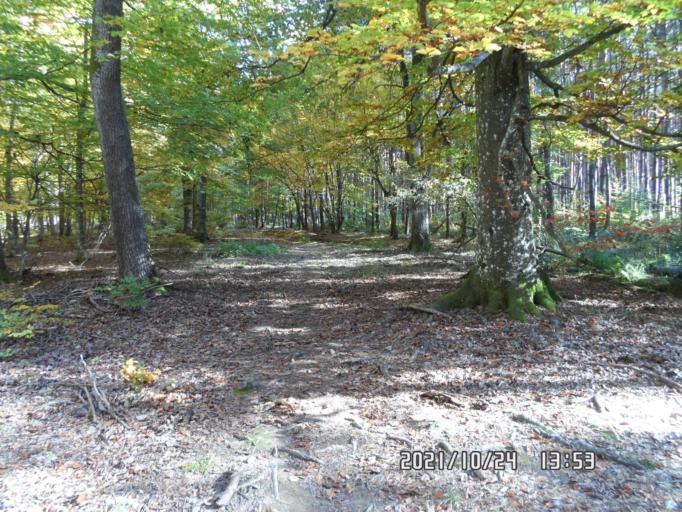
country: SI
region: Hodos-Hodos
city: Hodos
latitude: 46.7788
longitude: 16.3383
